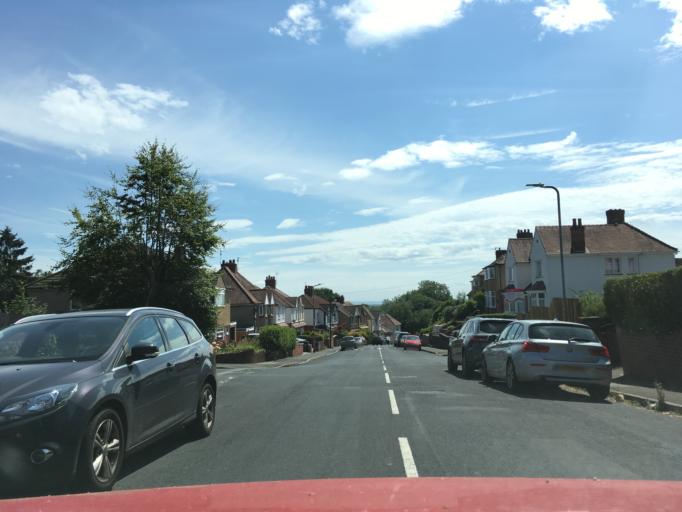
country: GB
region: Wales
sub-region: Newport
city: Newport
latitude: 51.5935
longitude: -3.0110
